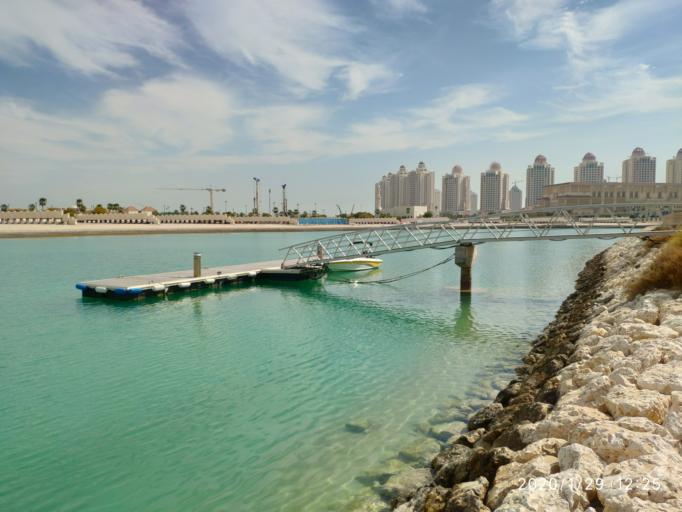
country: QA
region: Baladiyat ad Dawhah
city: Doha
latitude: 25.3769
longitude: 51.5505
